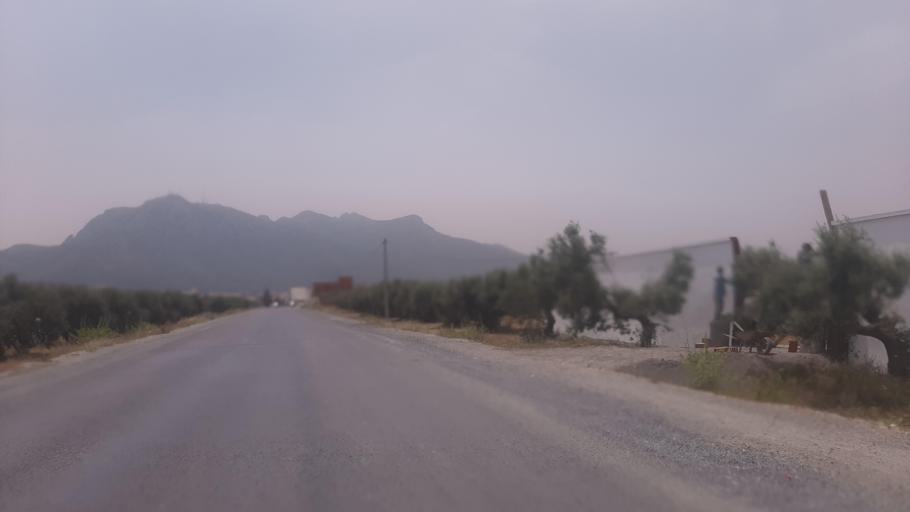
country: TN
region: Zaghwan
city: Zaghouan
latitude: 36.4195
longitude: 10.1368
